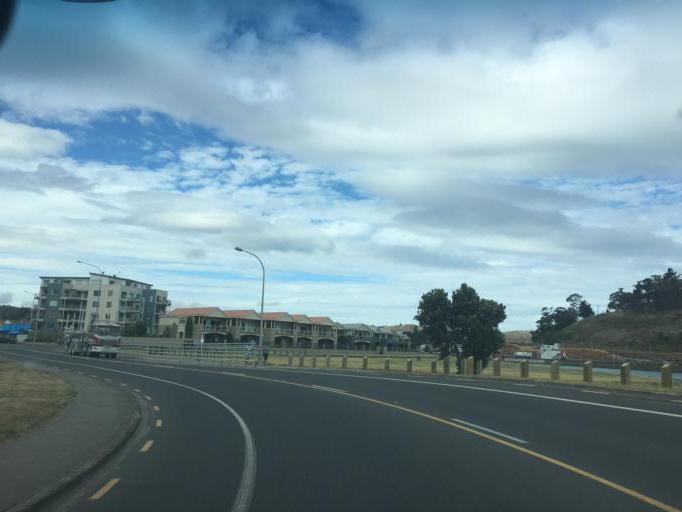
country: NZ
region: Gisborne
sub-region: Gisborne District
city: Gisborne
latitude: -38.6723
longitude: 178.0227
